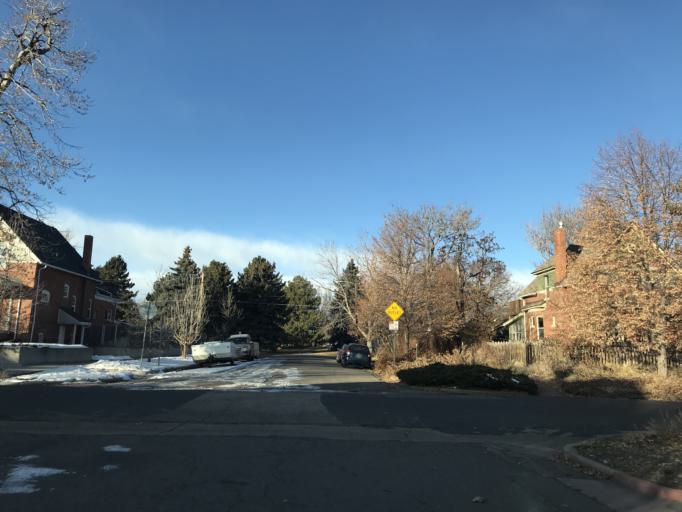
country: US
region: Colorado
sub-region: Denver County
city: Denver
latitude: 39.7595
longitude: -104.9632
